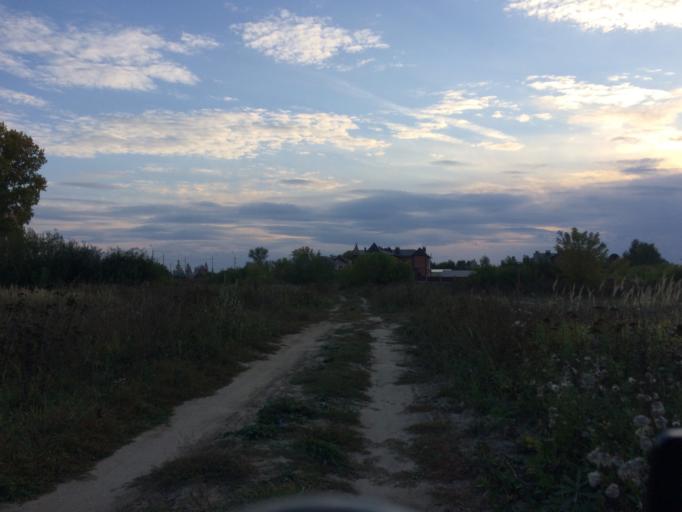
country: RU
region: Mariy-El
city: Yoshkar-Ola
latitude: 56.6453
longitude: 47.9190
